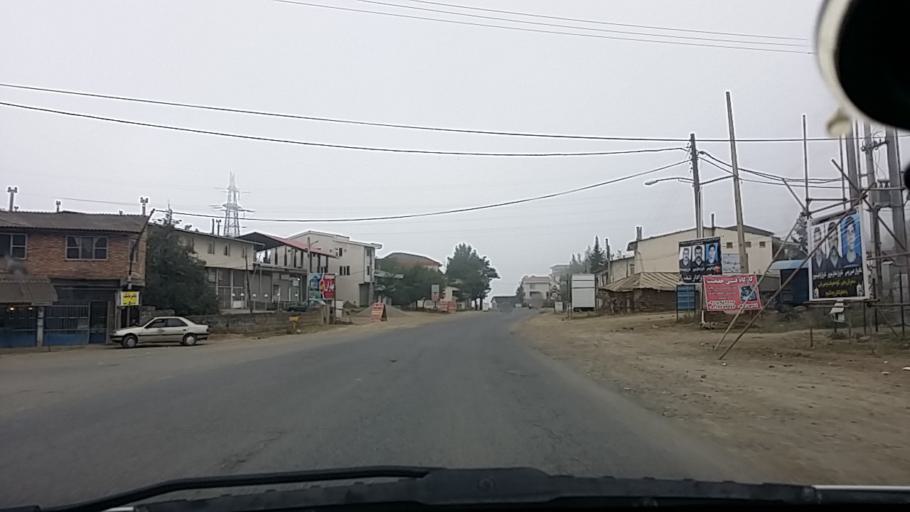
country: IR
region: Mazandaran
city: Chalus
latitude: 36.5111
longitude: 51.2464
